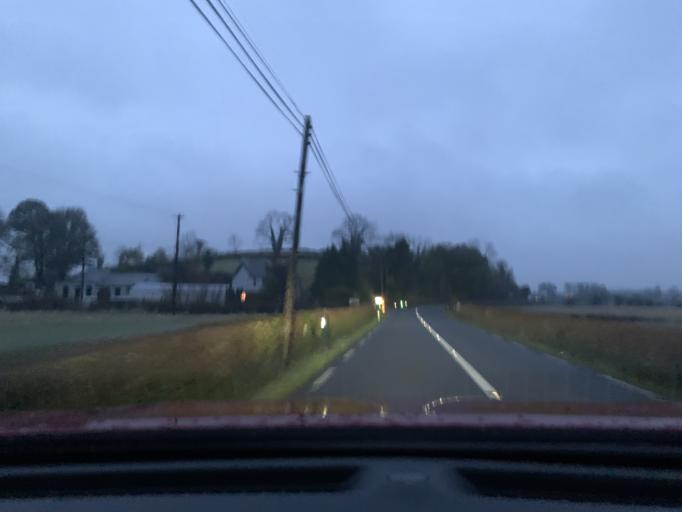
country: IE
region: Connaught
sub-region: Sligo
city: Ballymote
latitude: 54.0474
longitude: -8.5236
